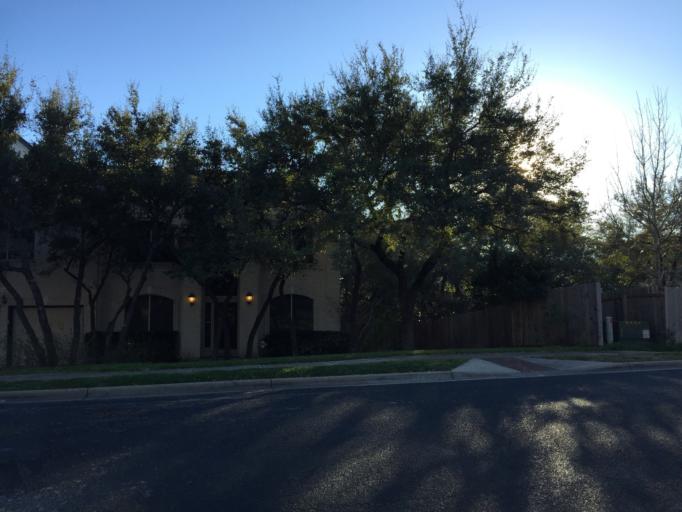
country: US
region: Texas
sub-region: Williamson County
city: Jollyville
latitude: 30.4345
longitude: -97.7856
